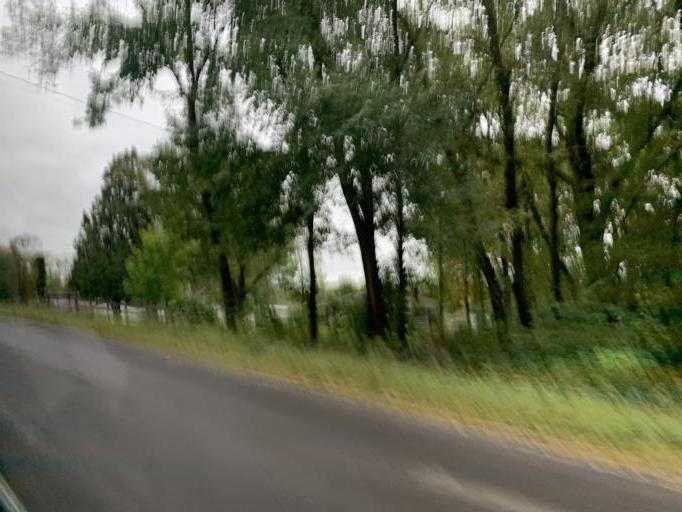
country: US
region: Wisconsin
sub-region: Grant County
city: Muscoda
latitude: 43.2049
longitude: -90.3876
